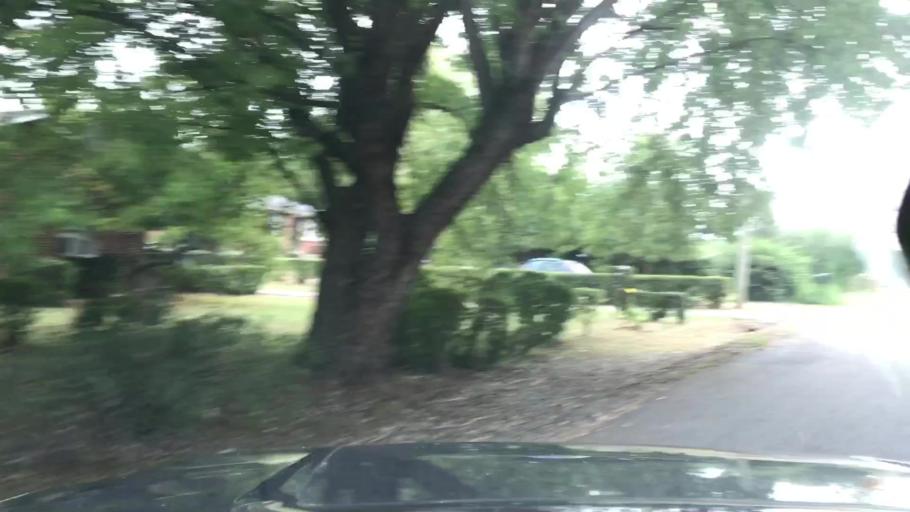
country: US
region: Tennessee
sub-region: Davidson County
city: Nashville
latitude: 36.2086
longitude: -86.8411
